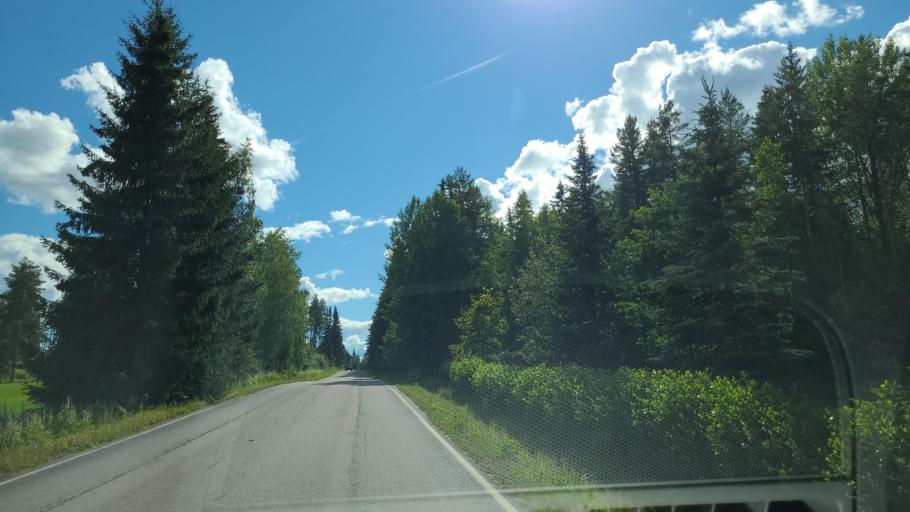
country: FI
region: Central Finland
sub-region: Jaemsae
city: Jaemsae
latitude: 61.8818
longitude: 25.2299
